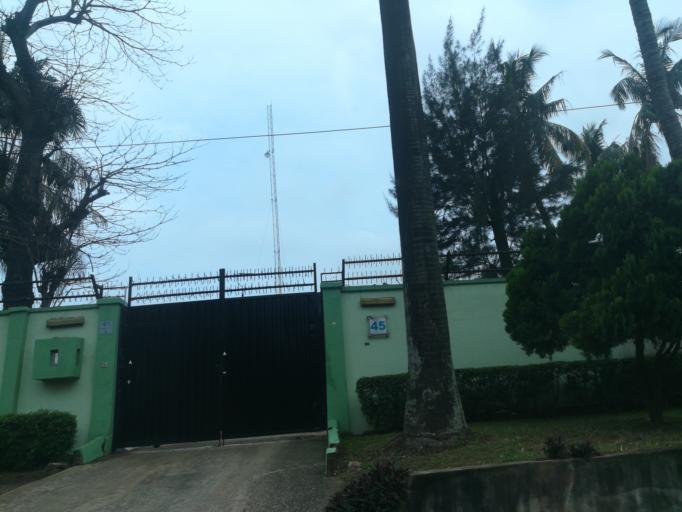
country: NG
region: Lagos
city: Oshodi
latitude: 6.5727
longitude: 3.3526
